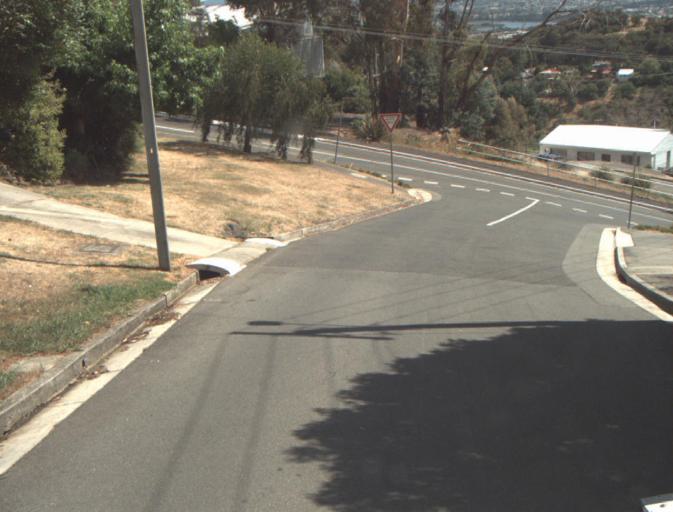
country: AU
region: Tasmania
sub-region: Launceston
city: West Launceston
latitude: -41.4504
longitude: 147.1241
